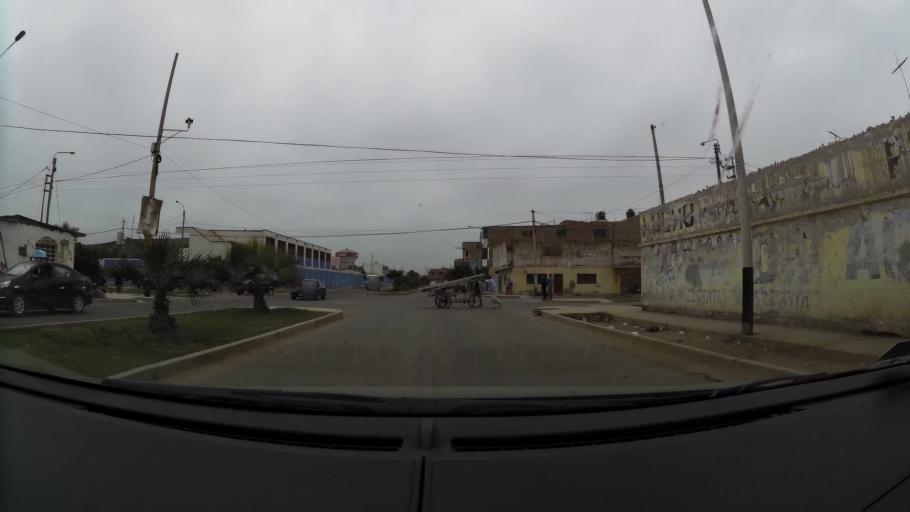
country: PE
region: La Libertad
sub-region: Provincia de Trujillo
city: Buenos Aires
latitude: -8.1456
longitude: -79.0509
